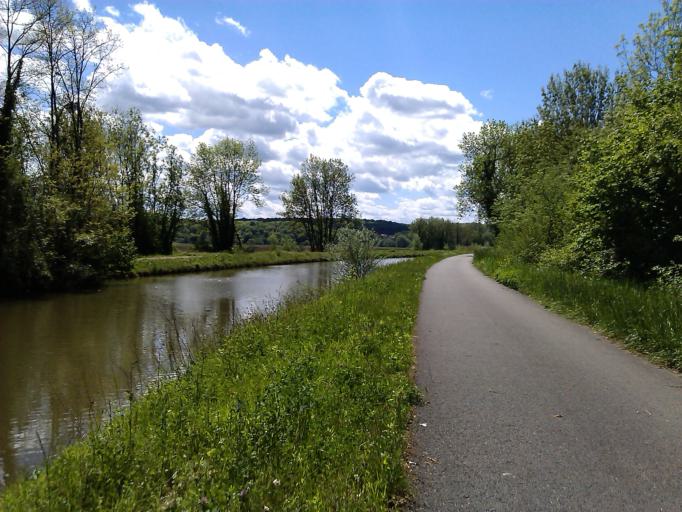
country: FR
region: Franche-Comte
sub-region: Territoire de Belfort
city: Mezire
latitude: 47.5388
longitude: 6.9105
